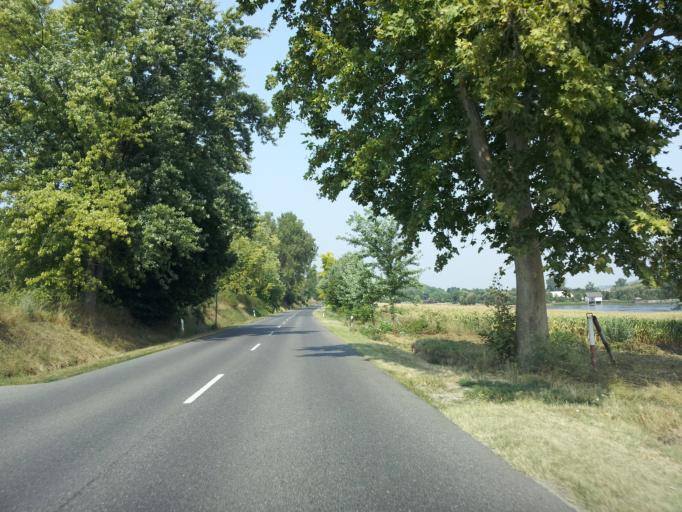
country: HU
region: Gyor-Moson-Sopron
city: Pannonhalma
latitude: 47.5051
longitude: 17.7660
